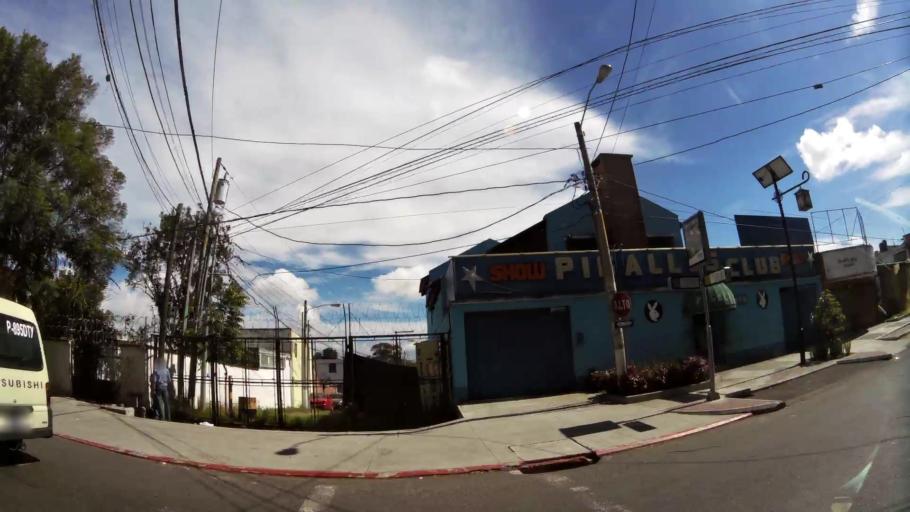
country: GT
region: Guatemala
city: Mixco
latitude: 14.6291
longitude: -90.5600
